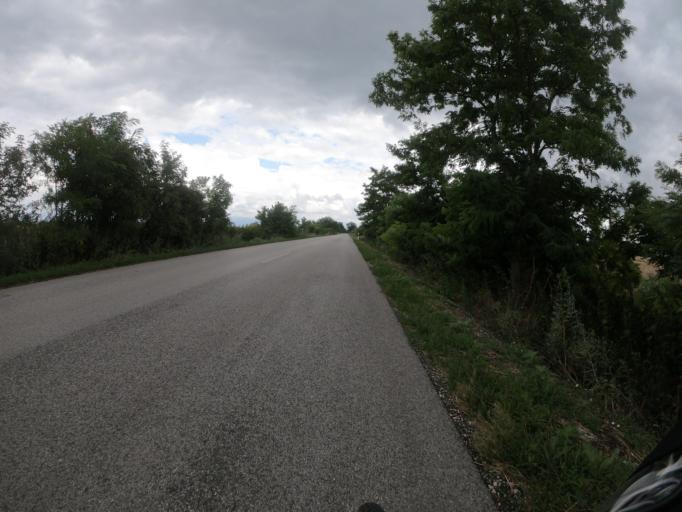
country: HU
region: Heves
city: Poroszlo
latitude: 47.6984
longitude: 20.7169
